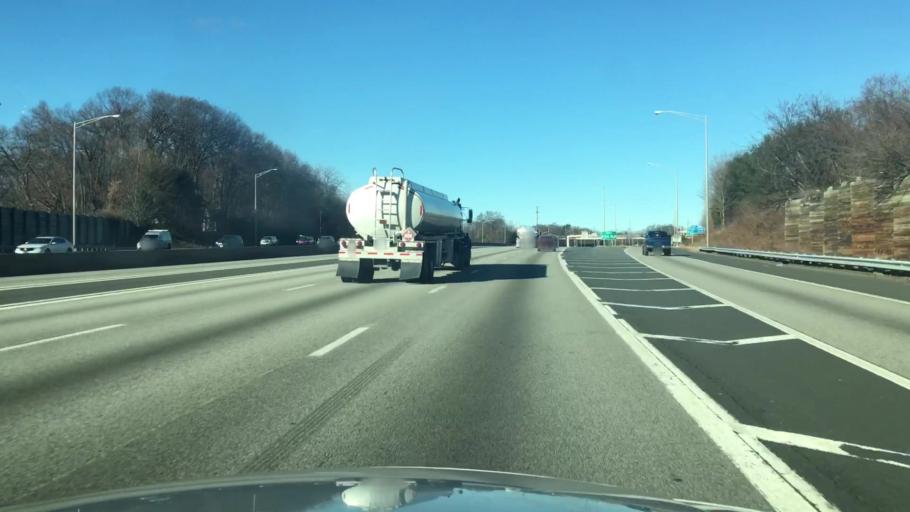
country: US
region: Connecticut
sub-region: Hartford County
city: Blue Hills
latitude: 41.8113
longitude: -72.6633
